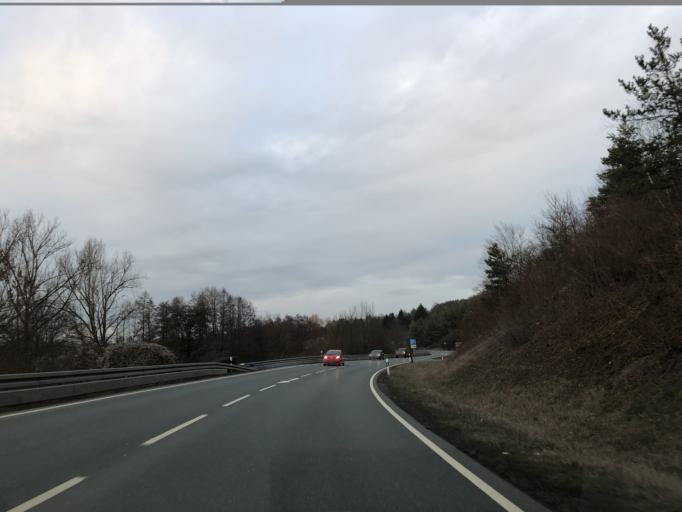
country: DE
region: Bavaria
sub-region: Regierungsbezirk Unterfranken
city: Marktheidenfeld
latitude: 49.8304
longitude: 9.6103
